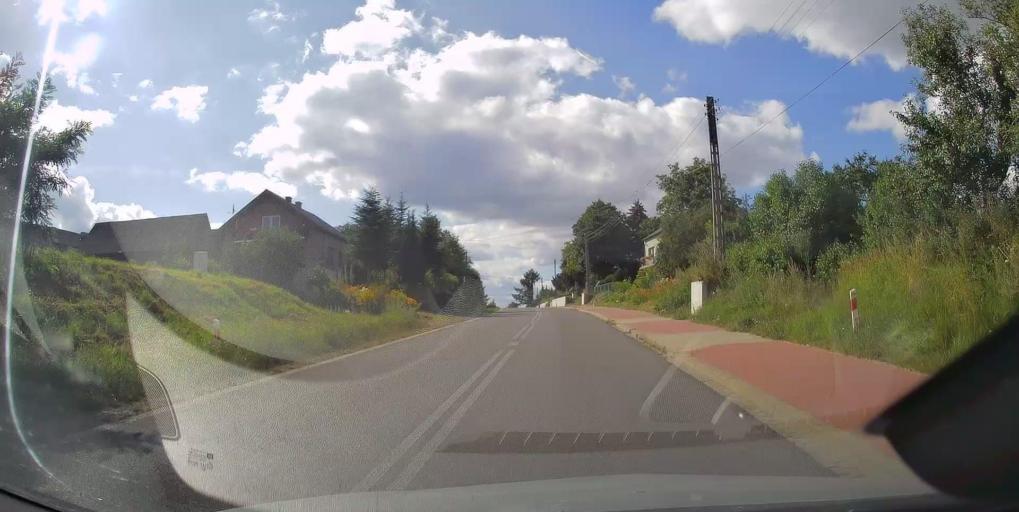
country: PL
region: Swietokrzyskie
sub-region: Powiat kielecki
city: Nowa Slupia
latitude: 50.8774
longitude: 21.0669
